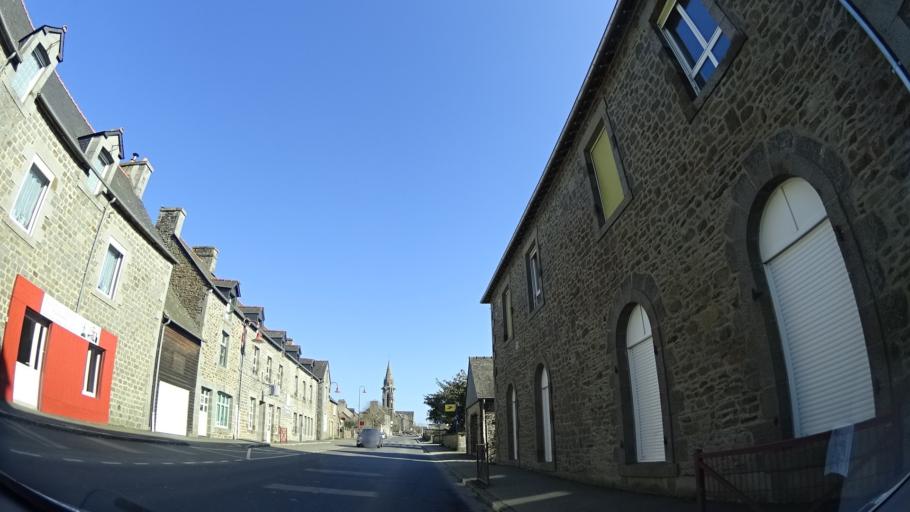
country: FR
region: Brittany
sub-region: Departement d'Ille-et-Vilaine
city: Meillac
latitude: 48.4121
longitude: -1.8158
